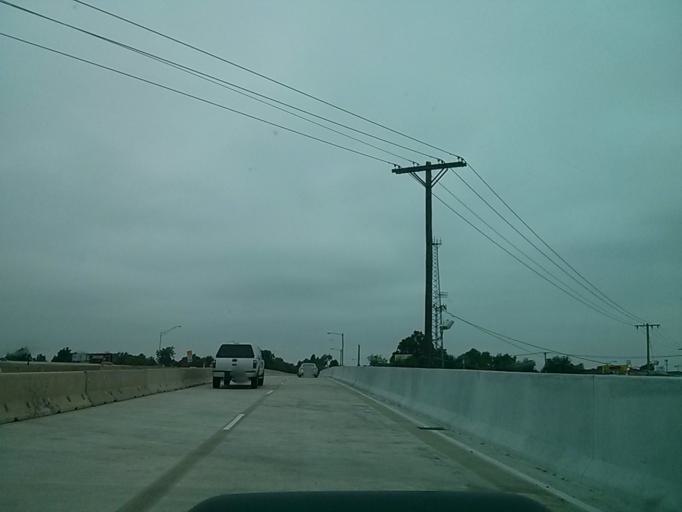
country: US
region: Oklahoma
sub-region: Tulsa County
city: Tulsa
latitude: 36.1610
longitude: -95.9144
